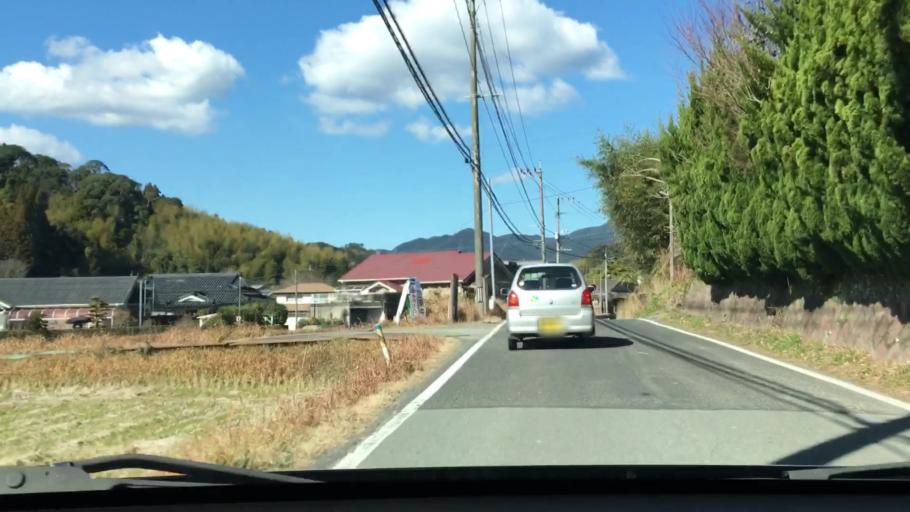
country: JP
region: Kagoshima
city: Ijuin
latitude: 31.6851
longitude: 130.4687
